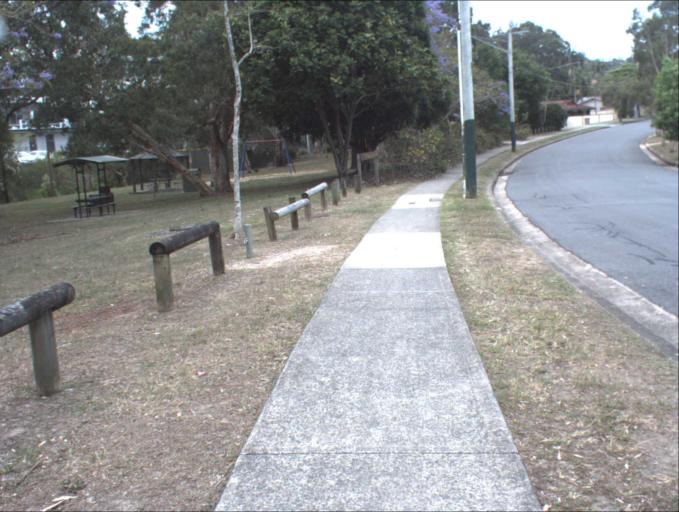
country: AU
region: Queensland
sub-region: Logan
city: Springwood
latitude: -27.6226
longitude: 153.1289
